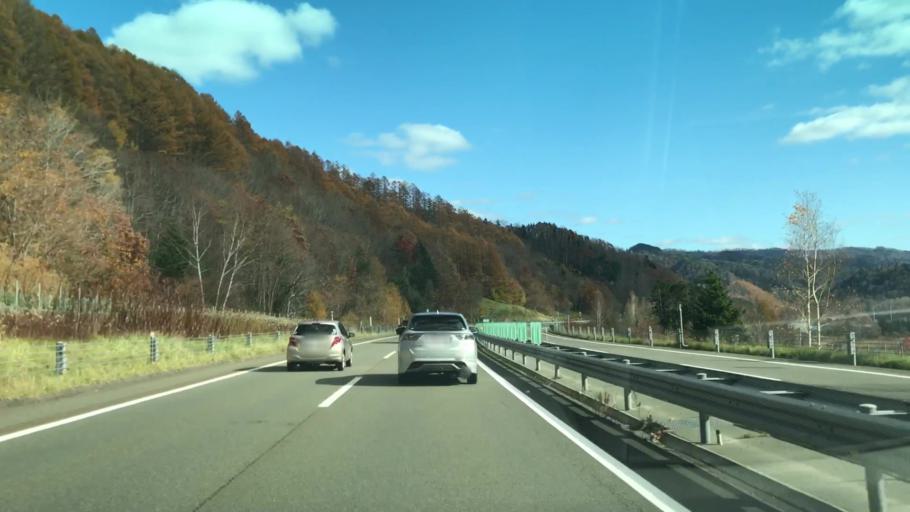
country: JP
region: Hokkaido
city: Chitose
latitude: 42.9081
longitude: 141.9925
